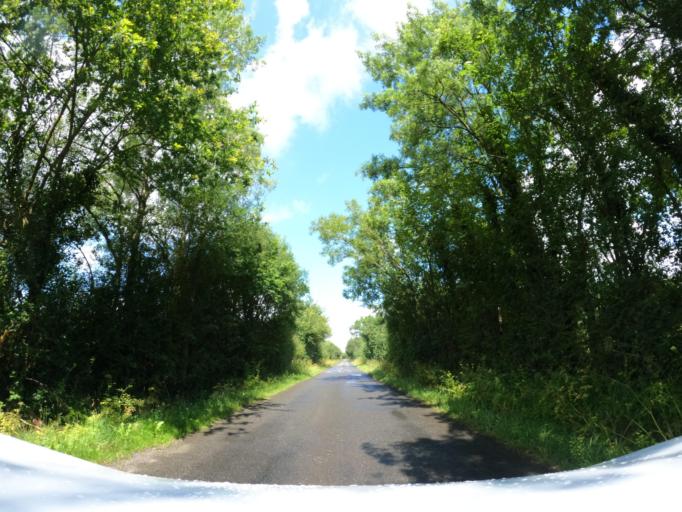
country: FR
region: Pays de la Loire
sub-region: Departement de la Loire-Atlantique
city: Saint-Mars-du-Desert
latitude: 47.3855
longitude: -1.3936
